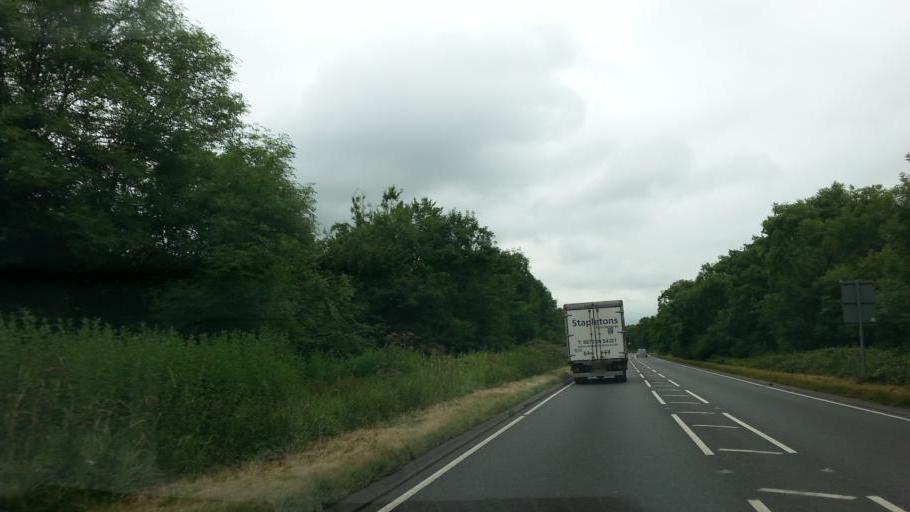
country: GB
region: England
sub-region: Northamptonshire
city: Broughton
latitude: 52.3157
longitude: -0.8083
